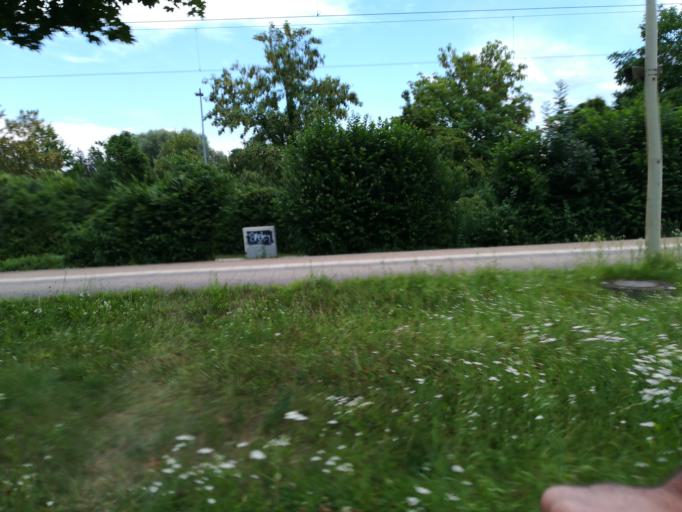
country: DE
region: Baden-Wuerttemberg
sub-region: Freiburg Region
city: Singen
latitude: 47.7599
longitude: 8.8271
